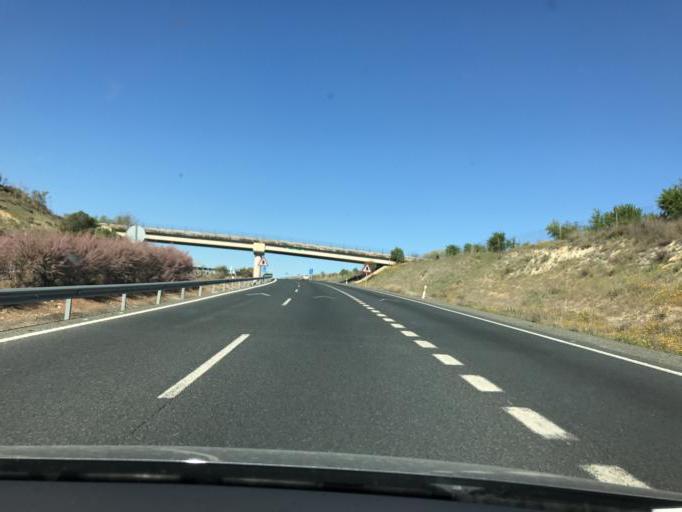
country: ES
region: Andalusia
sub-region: Provincia de Malaga
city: Villanueva de Tapia
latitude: 37.1465
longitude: -4.2484
